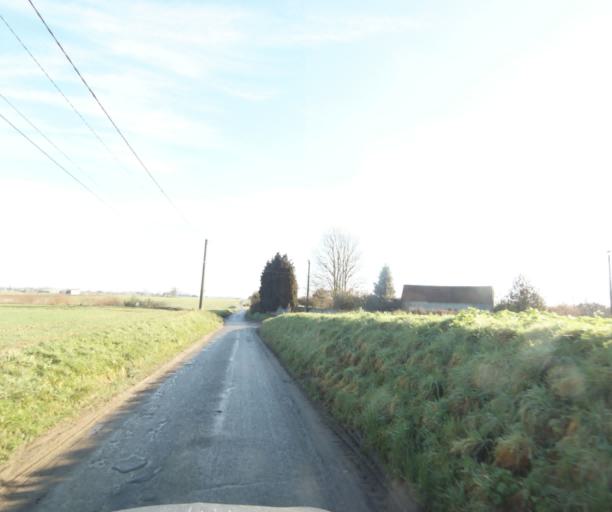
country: FR
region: Nord-Pas-de-Calais
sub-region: Departement du Nord
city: Aulnoy-lez-Valenciennes
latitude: 50.3303
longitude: 3.5483
